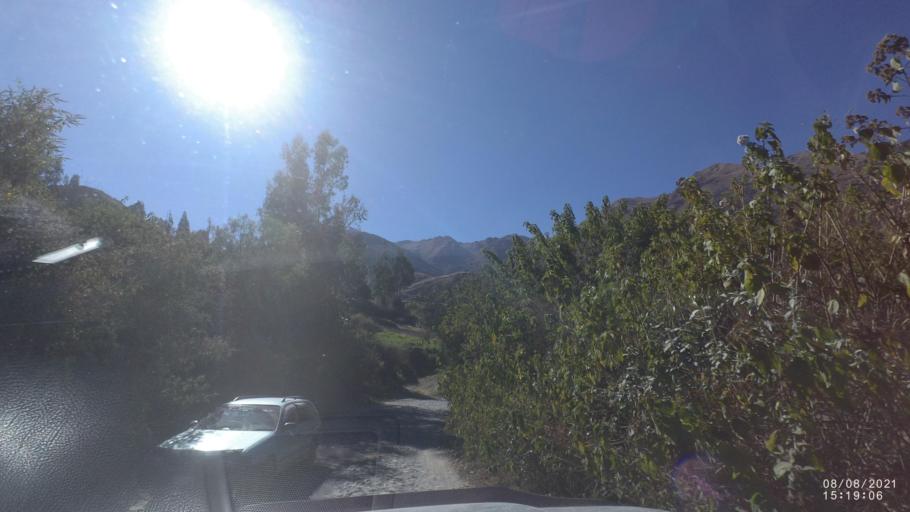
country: BO
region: Cochabamba
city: Cochabamba
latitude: -17.2897
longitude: -66.3004
